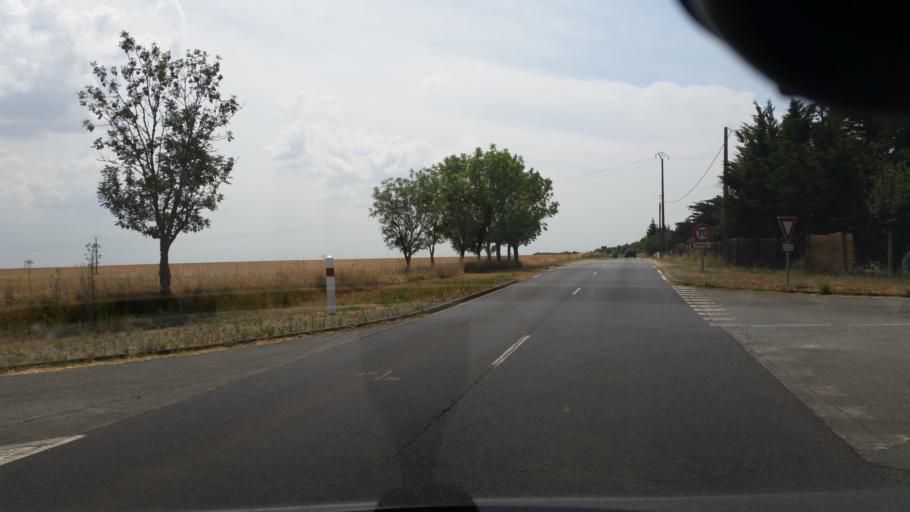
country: FR
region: Poitou-Charentes
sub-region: Departement de la Charente-Maritime
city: Saint-Jean-de-Liversay
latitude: 46.2119
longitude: -0.8756
